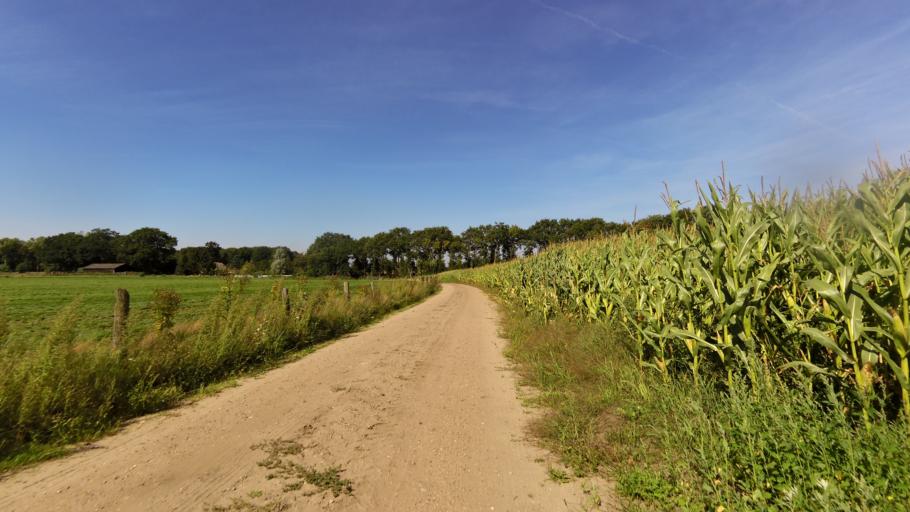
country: NL
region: Gelderland
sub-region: Gemeente Ede
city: Harskamp
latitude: 52.1339
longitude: 5.7631
